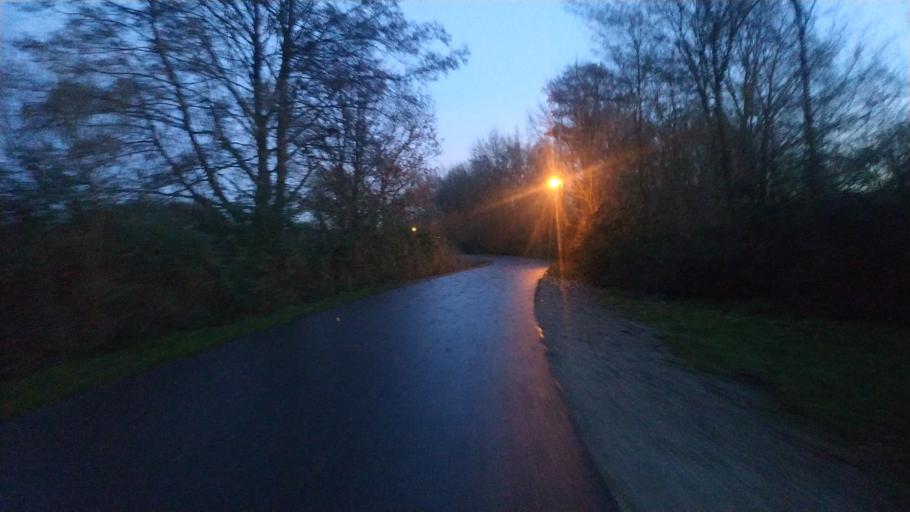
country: DE
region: North Rhine-Westphalia
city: Ibbenburen
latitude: 52.2667
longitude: 7.7234
